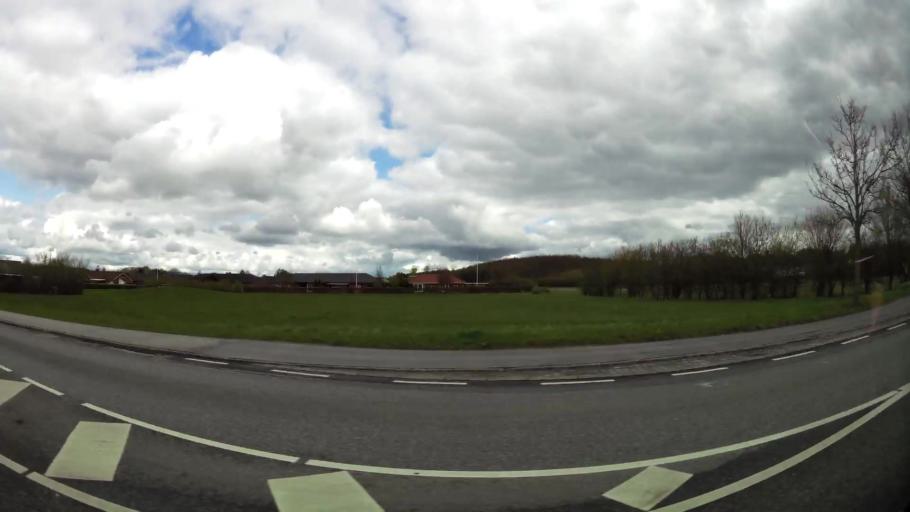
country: DK
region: South Denmark
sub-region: Haderslev Kommune
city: Vojens
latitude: 55.2421
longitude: 9.2586
